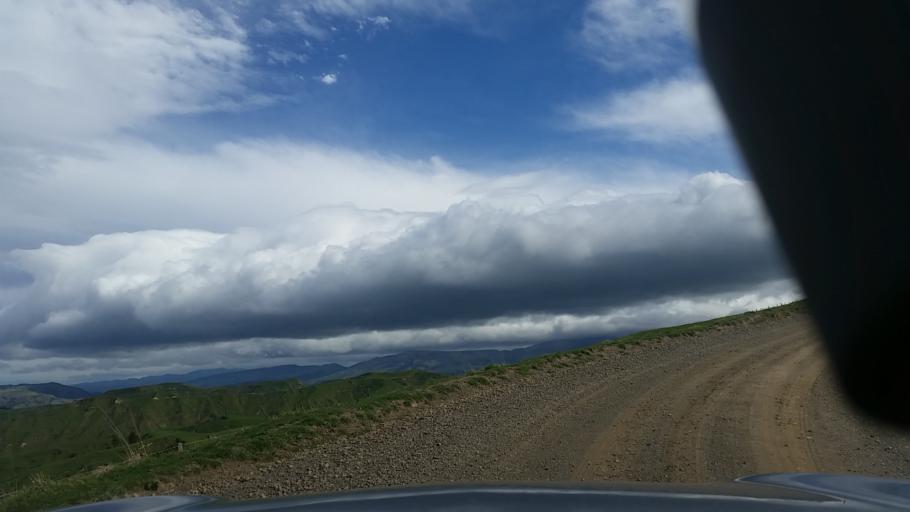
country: NZ
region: Hawke's Bay
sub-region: Napier City
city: Napier
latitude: -39.2109
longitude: 176.9593
